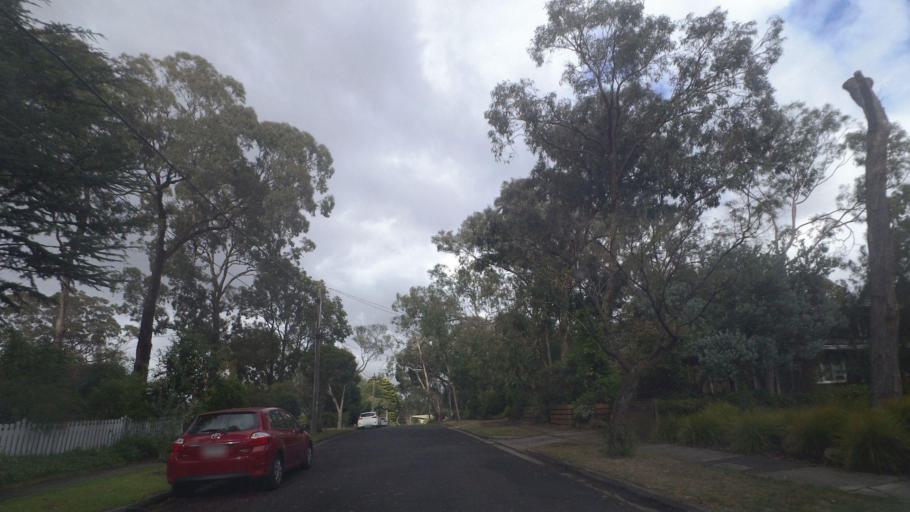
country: AU
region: Victoria
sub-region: Whitehorse
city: Forest Hill
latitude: -37.8306
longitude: 145.1617
